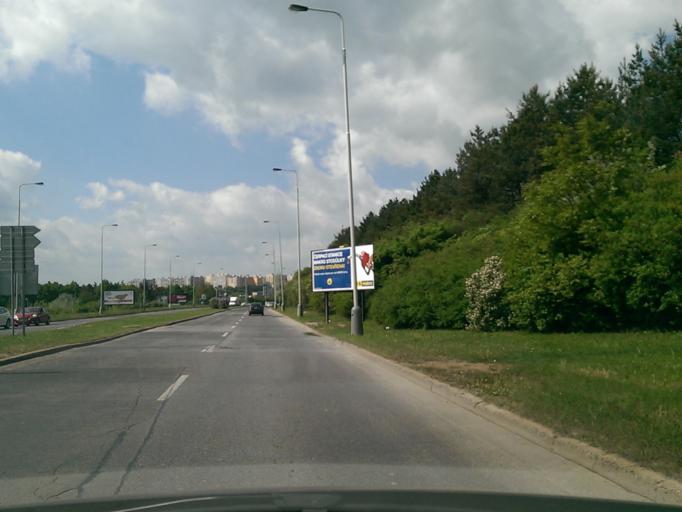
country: CZ
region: Praha
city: Branik
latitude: 50.0489
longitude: 14.3523
